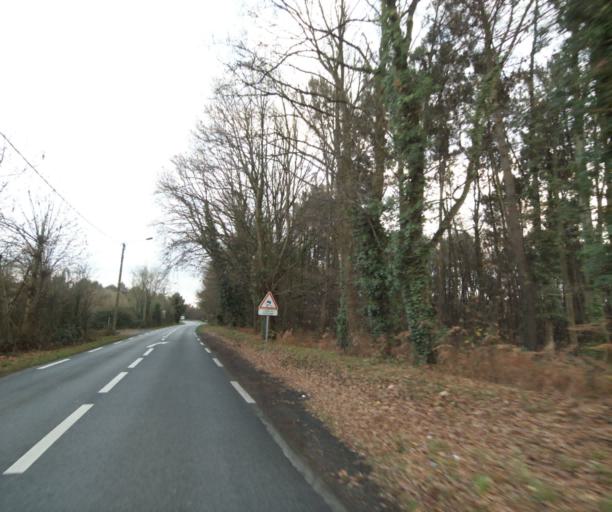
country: FR
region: Pays de la Loire
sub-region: Departement de la Sarthe
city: Le Mans
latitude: 47.9712
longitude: 0.2315
